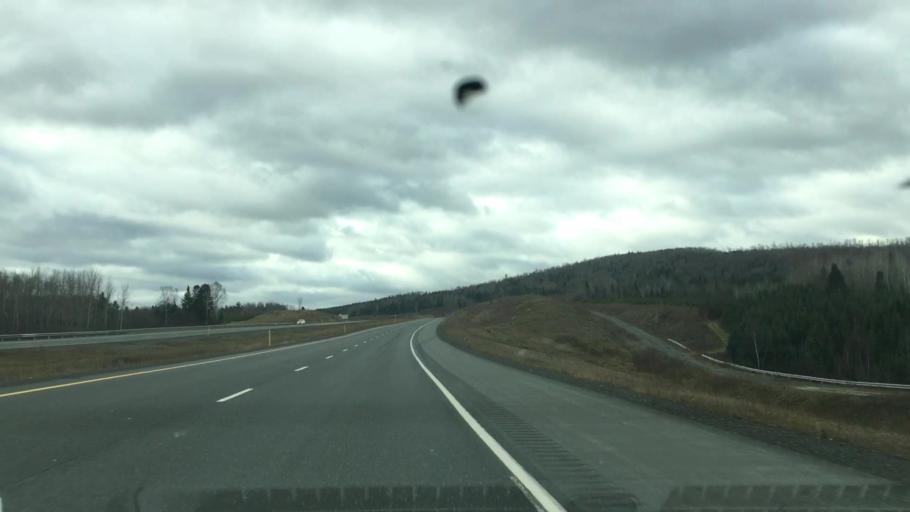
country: US
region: Maine
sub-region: Aroostook County
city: Fort Fairfield
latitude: 46.7328
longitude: -67.7218
